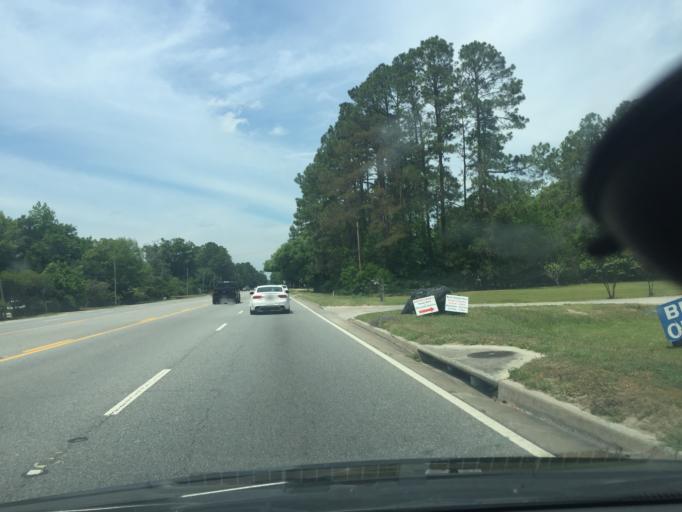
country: US
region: Georgia
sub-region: Chatham County
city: Bloomingdale
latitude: 32.1270
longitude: -81.2824
